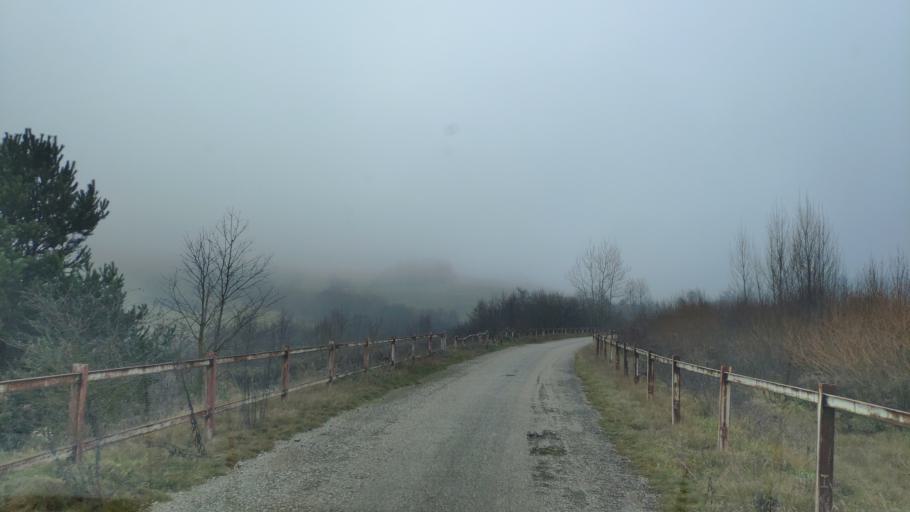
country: SK
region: Banskobystricky
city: Revuca
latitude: 48.6449
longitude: 20.2464
